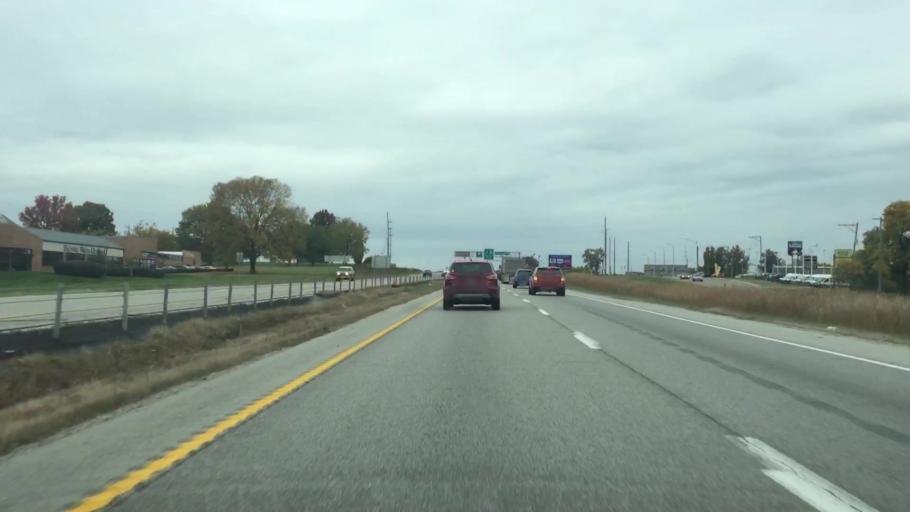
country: US
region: Missouri
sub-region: Jackson County
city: Lees Summit
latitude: 38.9193
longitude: -94.4016
